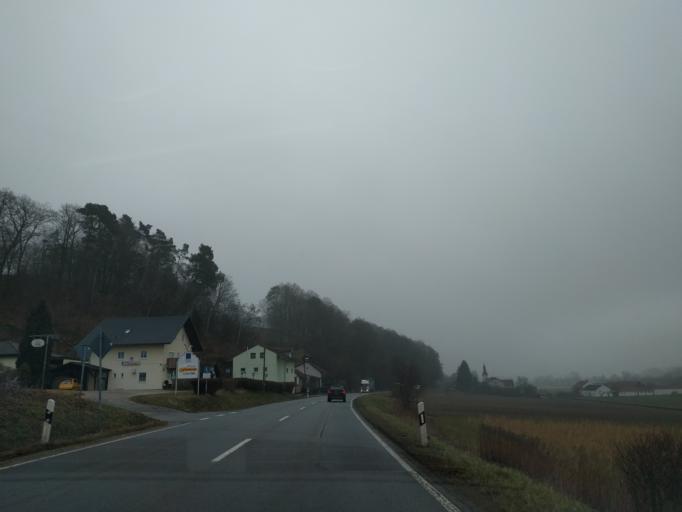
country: DE
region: Bavaria
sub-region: Lower Bavaria
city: Niederalteich
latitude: 48.8016
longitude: 12.9905
